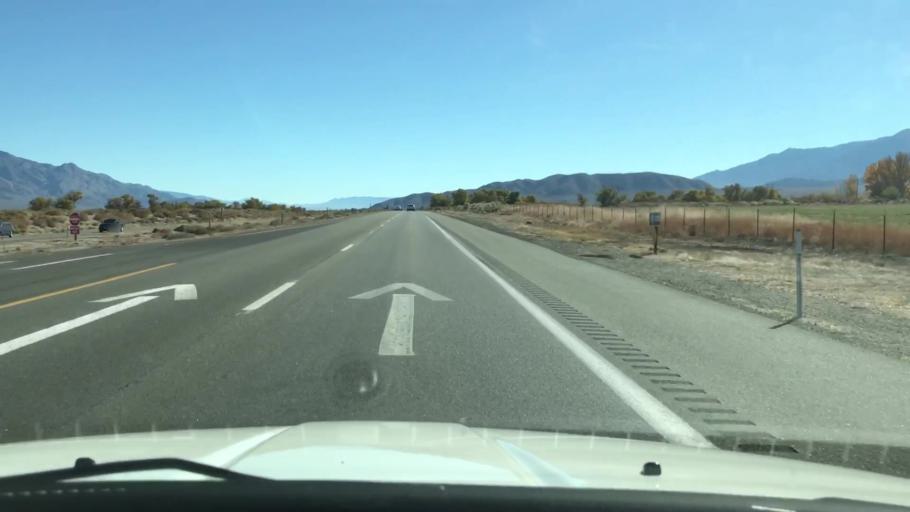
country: US
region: California
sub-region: Inyo County
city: Lone Pine
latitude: 36.7470
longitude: -118.1593
